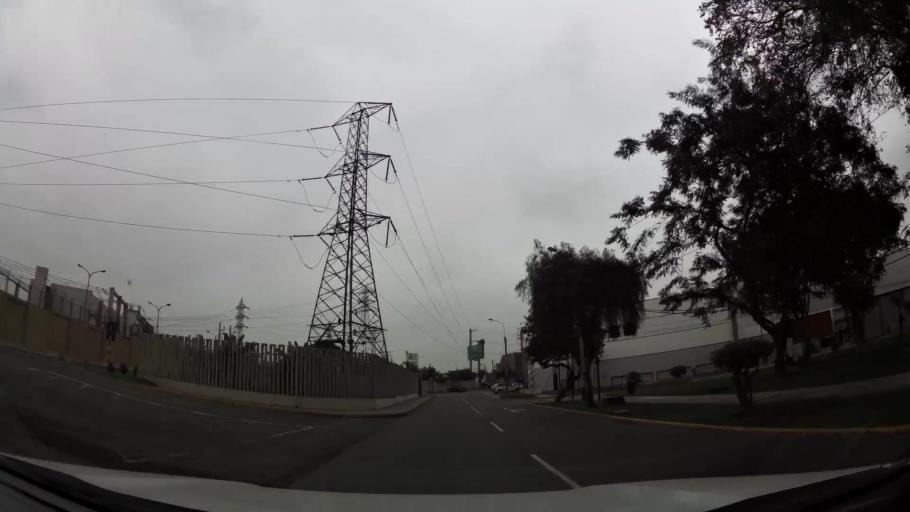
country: PE
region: Lima
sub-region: Lima
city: Surco
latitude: -12.1126
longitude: -76.9945
